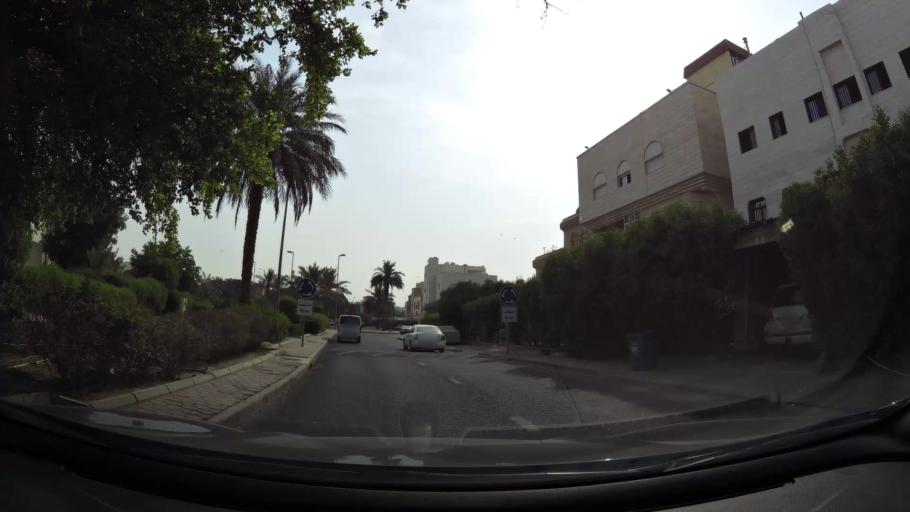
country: KW
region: Al Asimah
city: Ar Rabiyah
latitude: 29.2822
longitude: 47.9380
